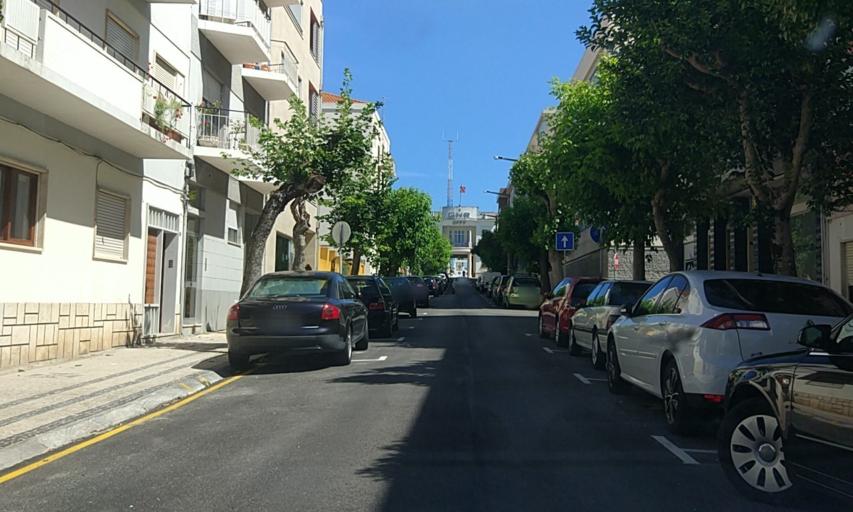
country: PT
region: Coimbra
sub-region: Figueira da Foz
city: Figueira da Foz
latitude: 40.1510
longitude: -8.8503
